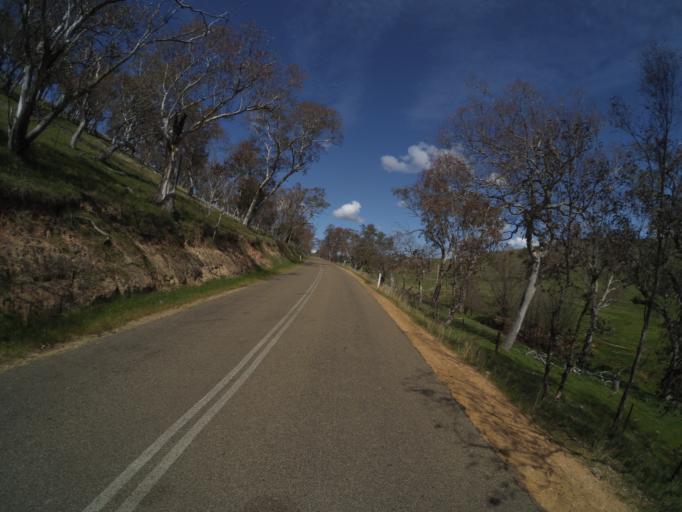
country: AU
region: New South Wales
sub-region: Yass Valley
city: Yass
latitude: -35.0066
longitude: 148.8488
